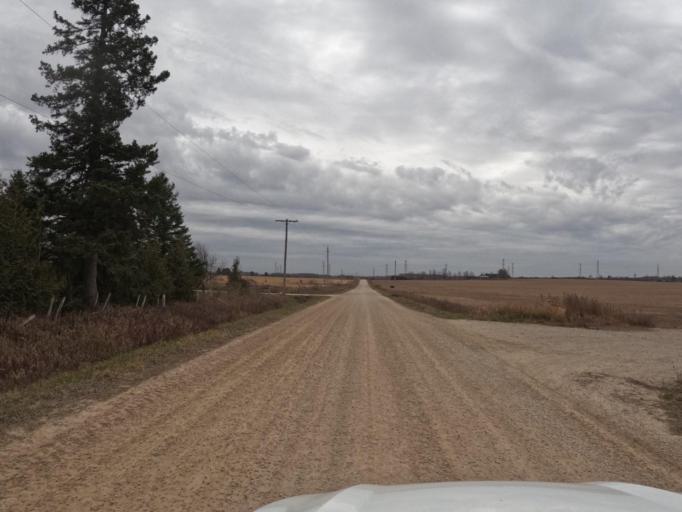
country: CA
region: Ontario
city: Shelburne
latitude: 44.0016
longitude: -80.3873
